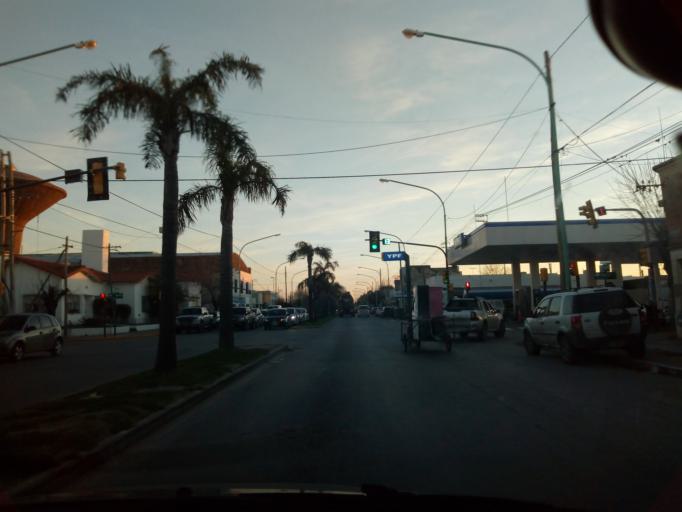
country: AR
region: Buenos Aires
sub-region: Partido de Ensenada
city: Ensenada
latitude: -34.8680
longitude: -57.9086
